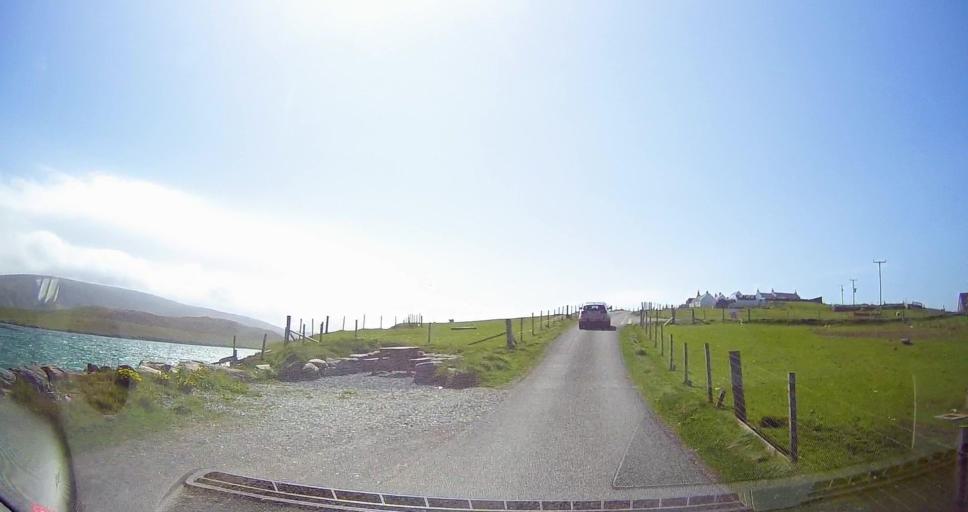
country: GB
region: Scotland
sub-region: Shetland Islands
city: Sandwick
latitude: 60.0641
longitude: -1.3402
